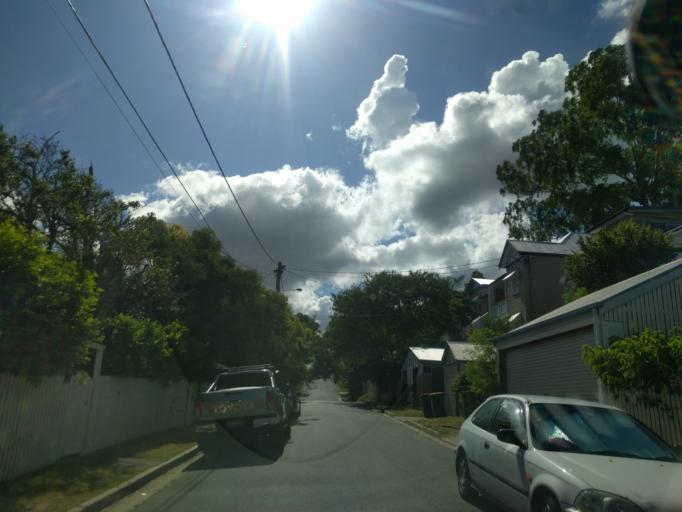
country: AU
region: Queensland
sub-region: Brisbane
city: Milton
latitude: -27.4697
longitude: 152.9918
